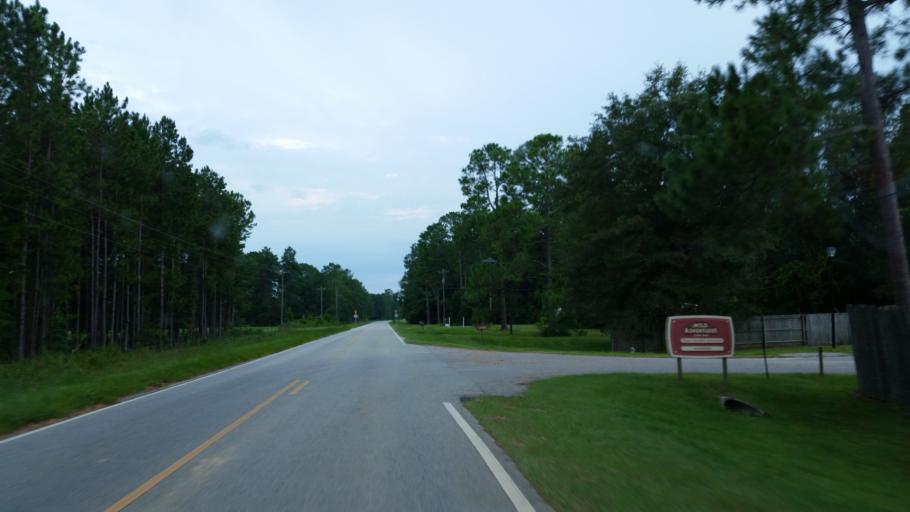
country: US
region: Georgia
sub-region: Lowndes County
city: Valdosta
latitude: 30.7202
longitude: -83.3186
